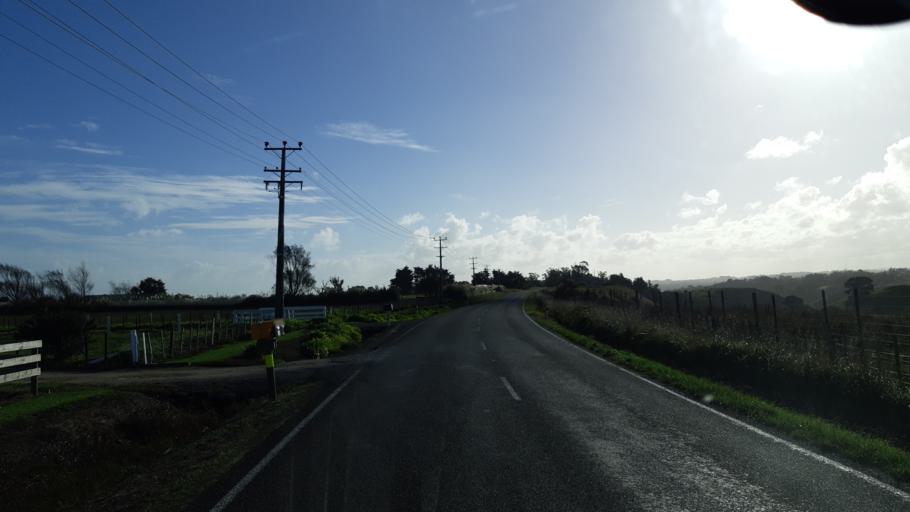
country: NZ
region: Manawatu-Wanganui
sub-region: Wanganui District
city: Wanganui
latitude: -39.9421
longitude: 175.0889
